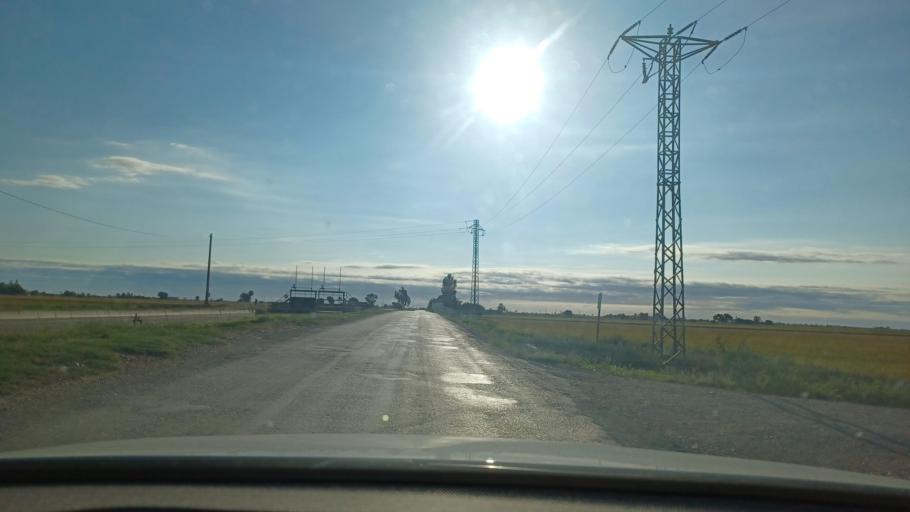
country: ES
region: Catalonia
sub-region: Provincia de Tarragona
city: Amposta
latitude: 40.7000
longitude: 0.6071
